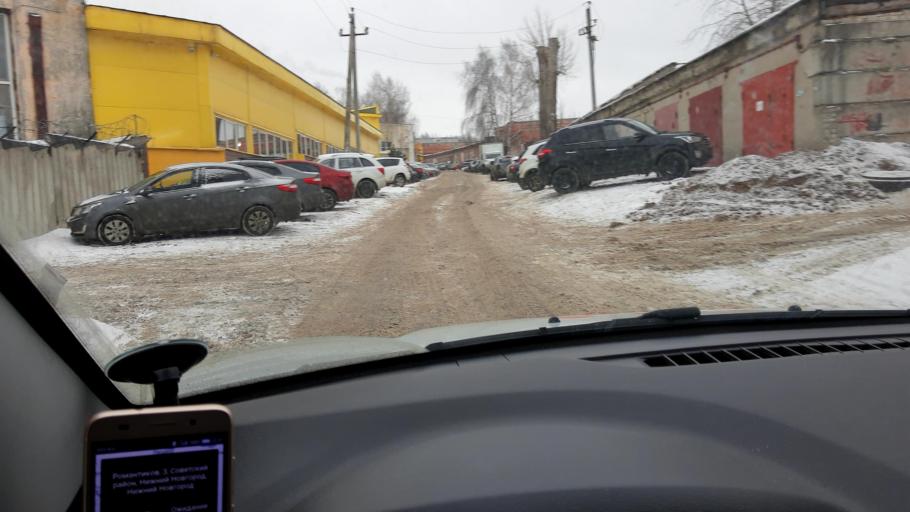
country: RU
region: Nizjnij Novgorod
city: Nizhniy Novgorod
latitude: 56.2476
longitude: 43.9611
